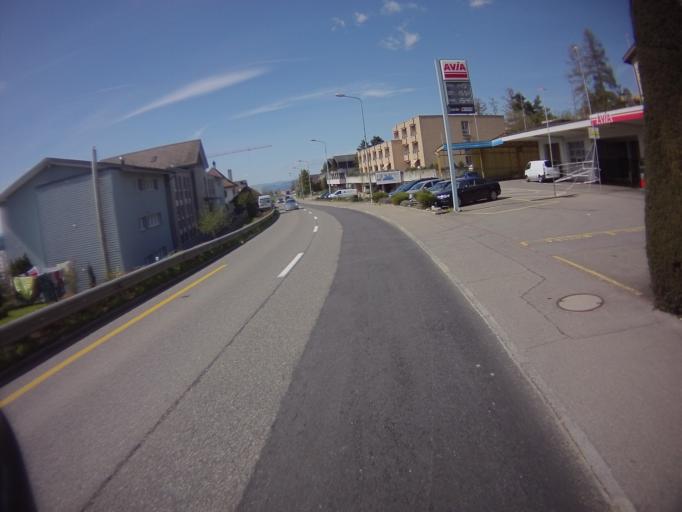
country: CH
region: Aargau
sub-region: Bezirk Baden
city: Kunten
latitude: 47.3864
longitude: 8.3463
